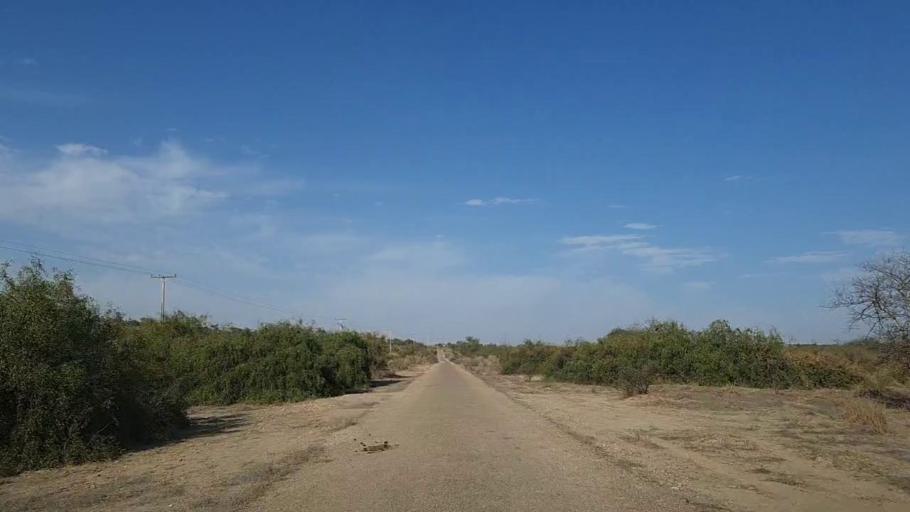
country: PK
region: Sindh
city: Naukot
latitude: 24.8522
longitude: 69.5206
